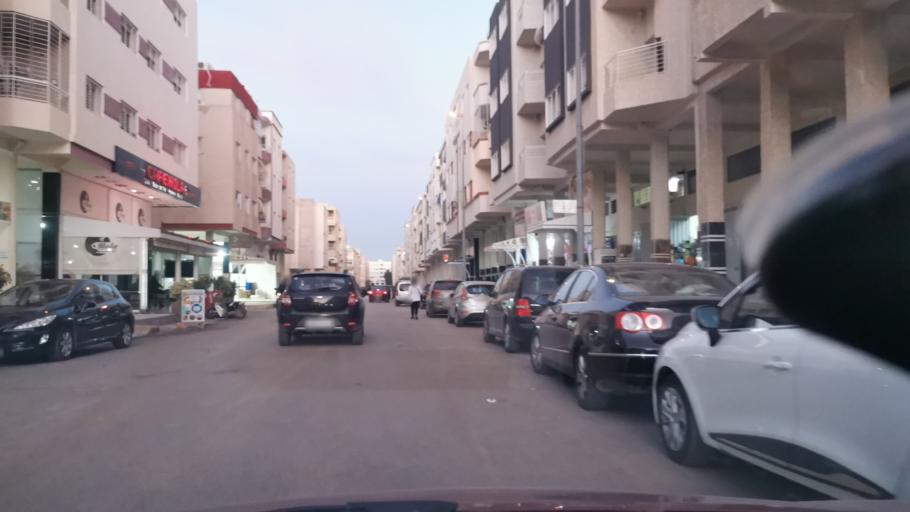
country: MA
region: Fes-Boulemane
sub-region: Fes
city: Fes
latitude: 34.0077
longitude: -4.9687
